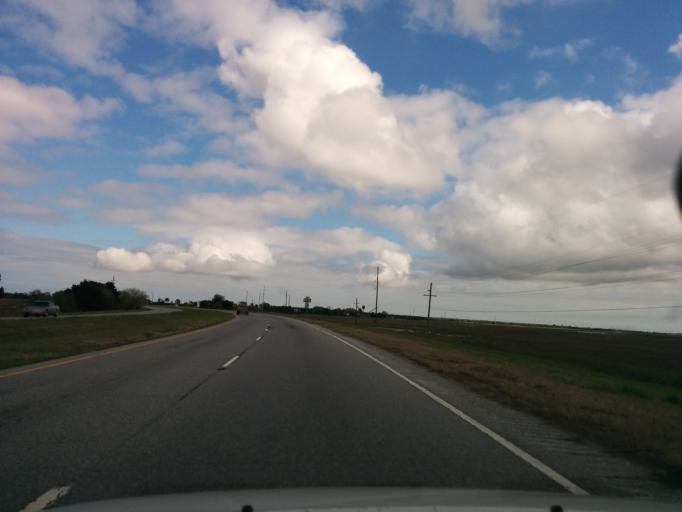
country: US
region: Georgia
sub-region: Glynn County
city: Brunswick
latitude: 31.1054
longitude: -81.4992
